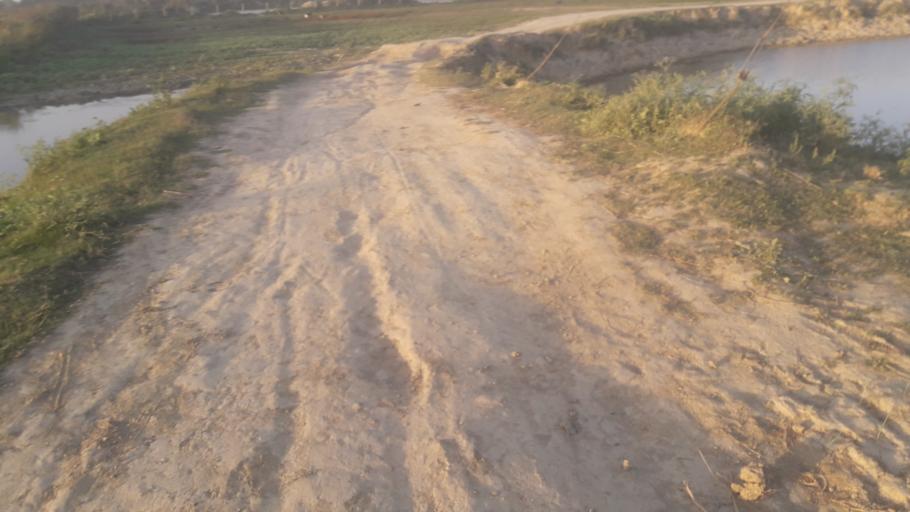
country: NP
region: Eastern Region
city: Siraha
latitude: 26.6314
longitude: 86.1935
